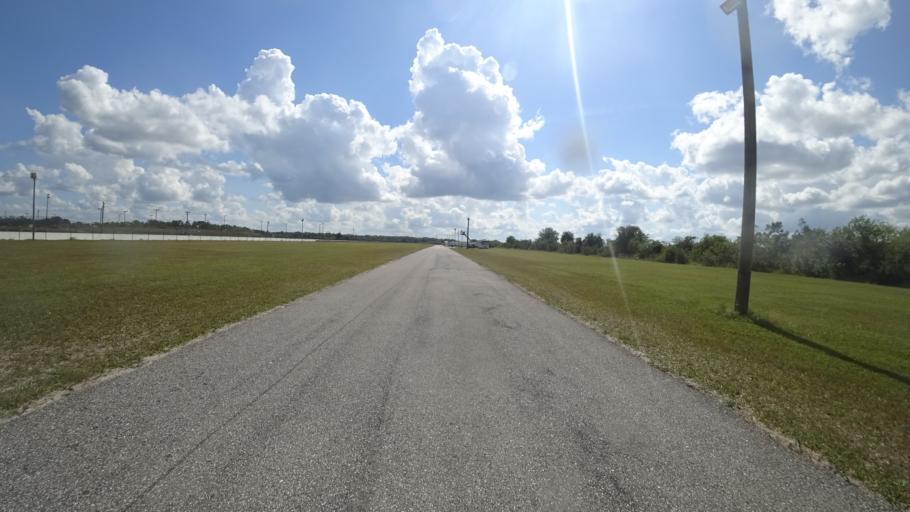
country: US
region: Florida
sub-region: Sarasota County
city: The Meadows
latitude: 27.4675
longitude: -82.3274
